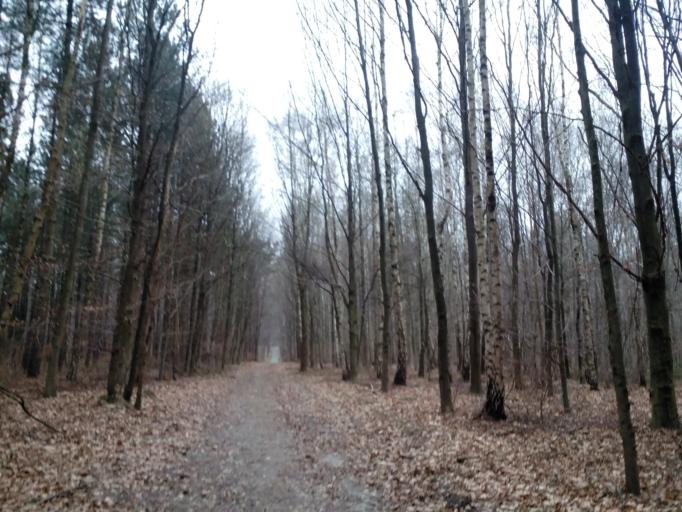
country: BE
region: Flanders
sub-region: Provincie Vlaams-Brabant
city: Bierbeek
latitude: 50.8069
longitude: 4.7187
